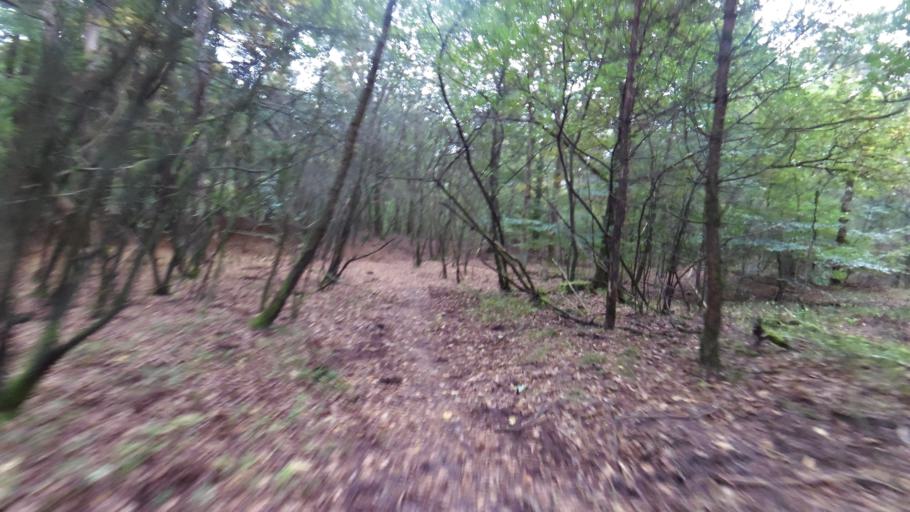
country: NL
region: Gelderland
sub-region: Gemeente Ede
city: Harskamp
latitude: 52.1735
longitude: 5.8314
